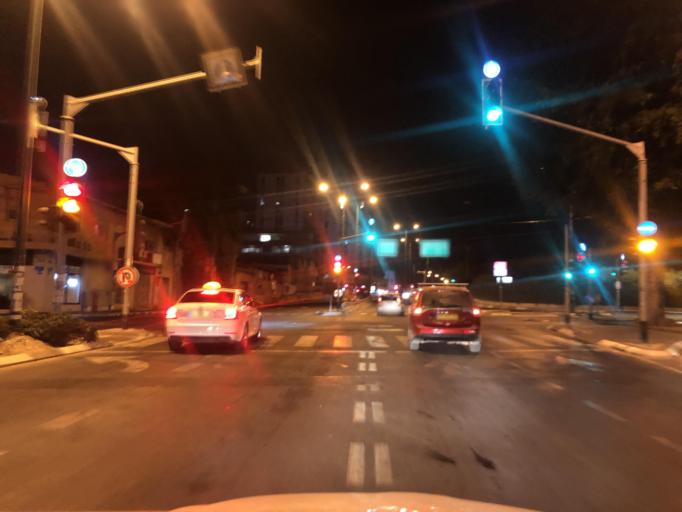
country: IL
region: Tel Aviv
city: Yafo
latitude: 32.0514
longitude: 34.7695
